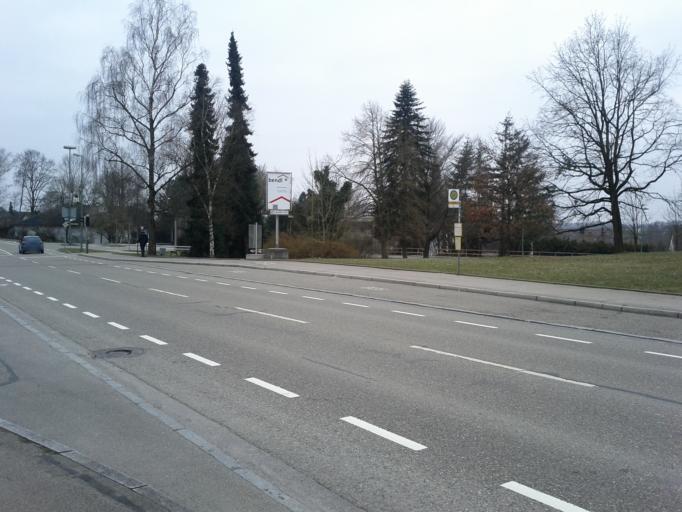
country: DE
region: Bavaria
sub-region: Swabia
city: Guenzburg
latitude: 48.4487
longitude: 10.2804
